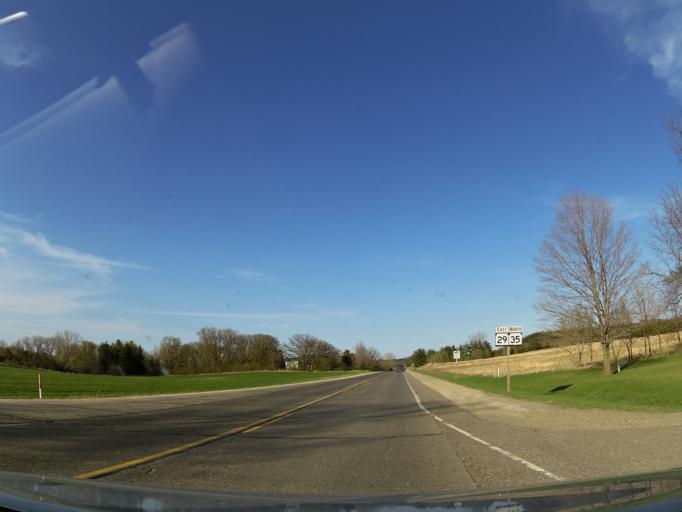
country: US
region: Wisconsin
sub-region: Pierce County
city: River Falls
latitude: 44.8217
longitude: -92.6446
